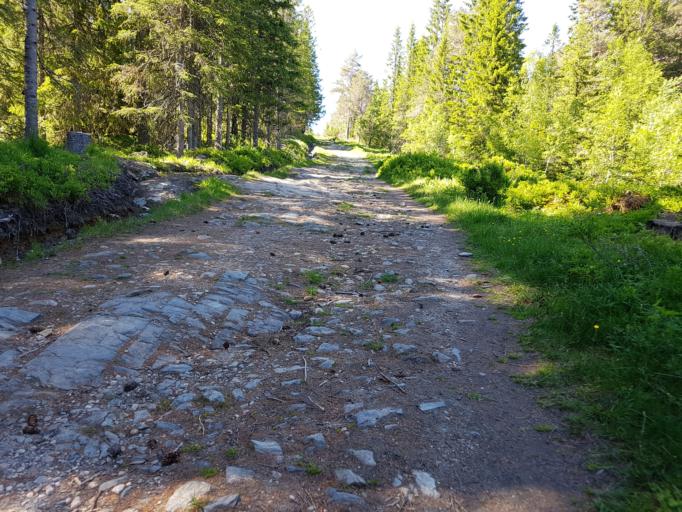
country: NO
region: Sor-Trondelag
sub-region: Trondheim
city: Trondheim
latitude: 63.4261
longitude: 10.2996
